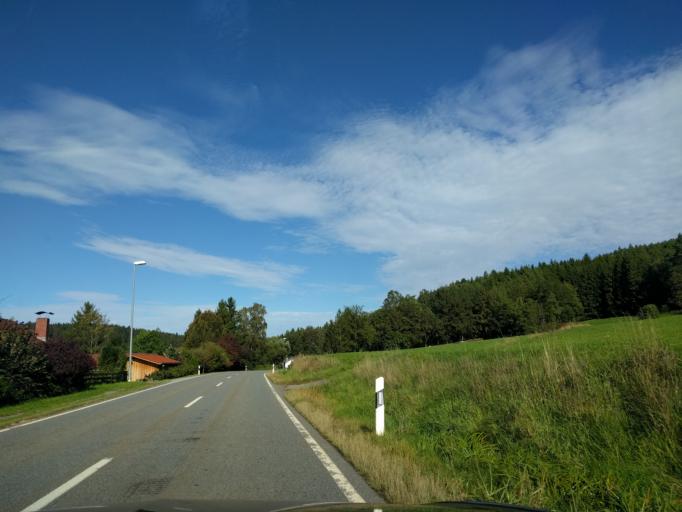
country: DE
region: Bavaria
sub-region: Lower Bavaria
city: Viechtach
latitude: 49.1059
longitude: 12.8845
